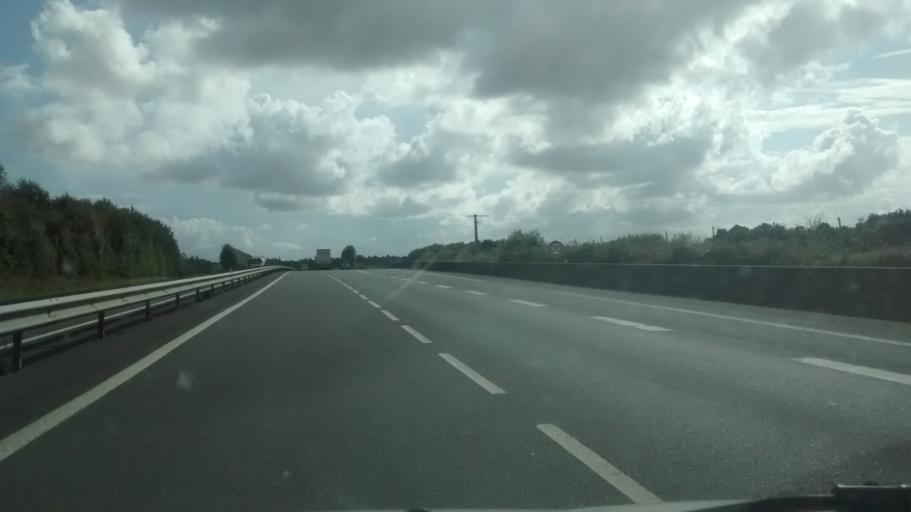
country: FR
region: Lower Normandy
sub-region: Departement du Calvados
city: Saint-Martin-des-Besaces
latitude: 49.0279
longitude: -0.8289
